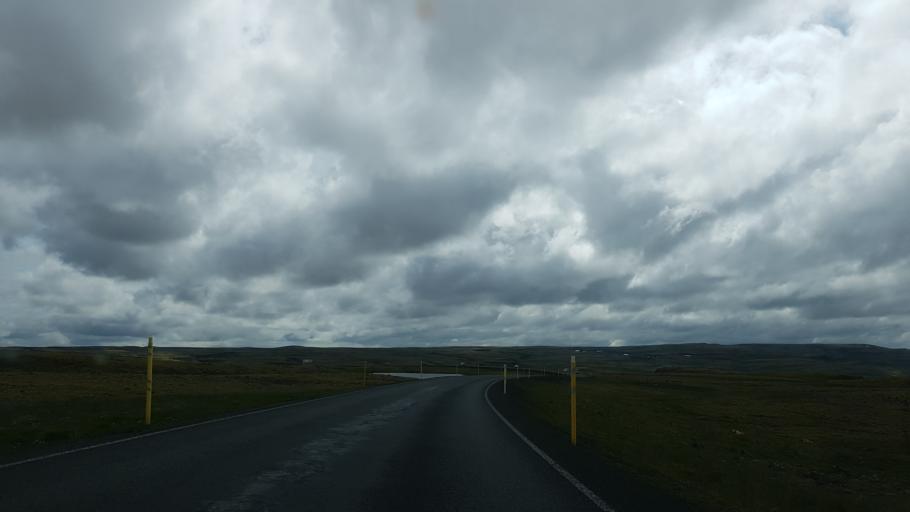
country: IS
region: West
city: Borgarnes
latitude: 64.9504
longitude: -21.0558
